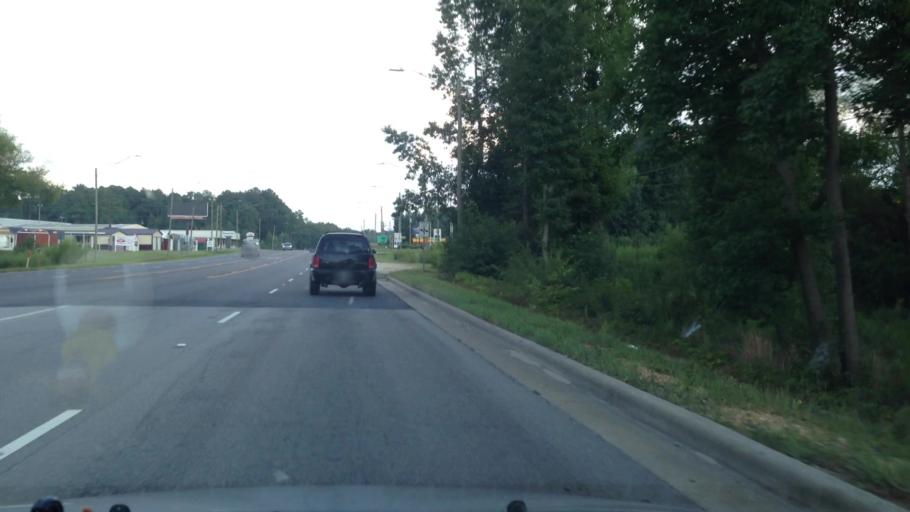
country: US
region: North Carolina
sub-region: Harnett County
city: Lillington
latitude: 35.4171
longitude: -78.8018
